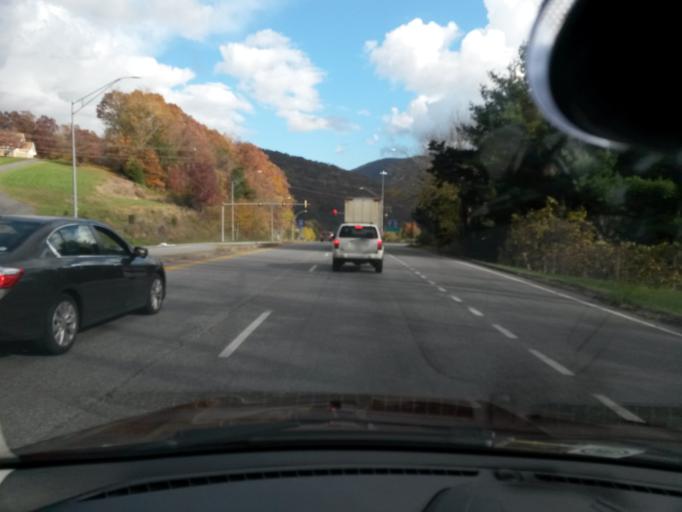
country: US
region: Virginia
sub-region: City of Covington
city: Fairlawn
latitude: 37.7779
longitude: -79.9765
